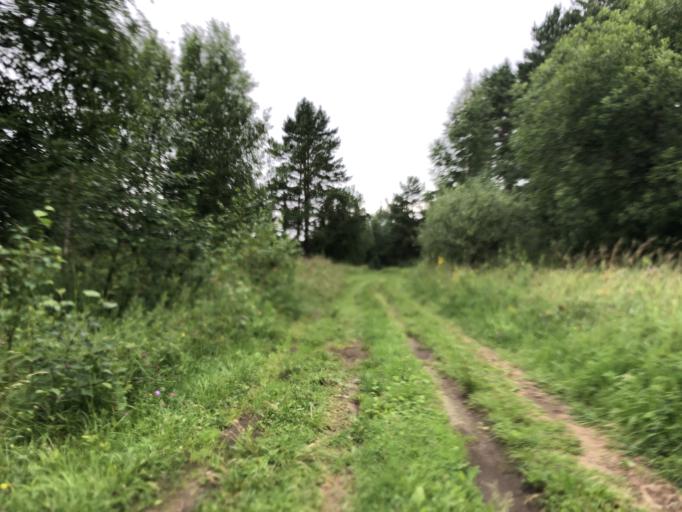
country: RU
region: Tverskaya
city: Rzhev
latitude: 56.2469
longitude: 34.3692
